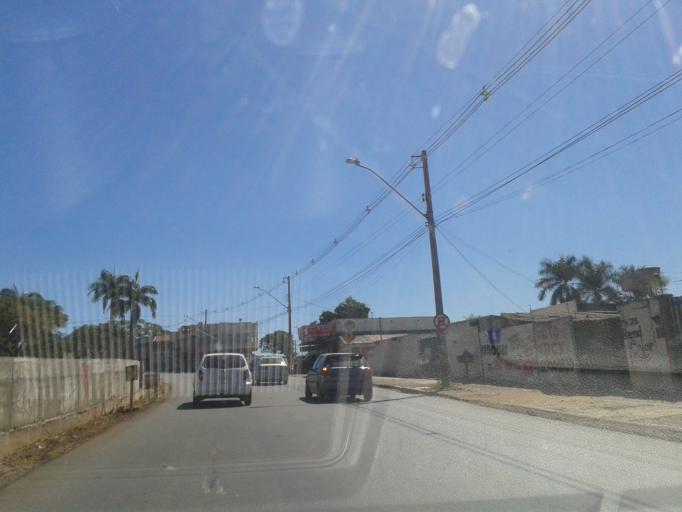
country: BR
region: Goias
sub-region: Goiania
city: Goiania
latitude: -16.6412
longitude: -49.2684
